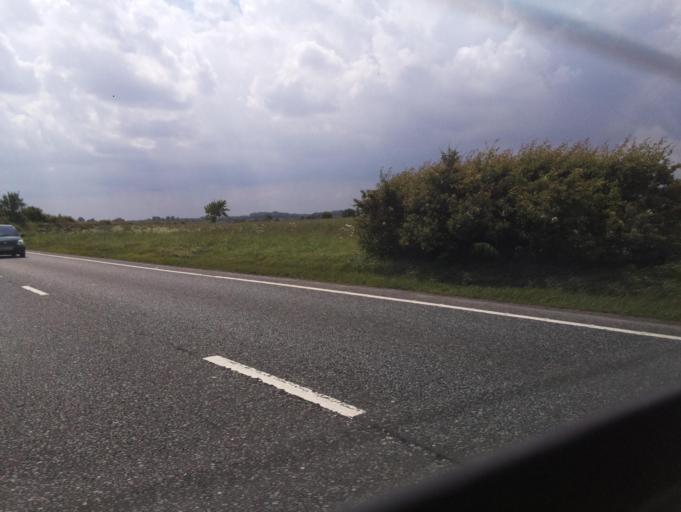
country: GB
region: England
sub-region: North Yorkshire
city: Thirsk
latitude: 54.2710
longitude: -1.3444
